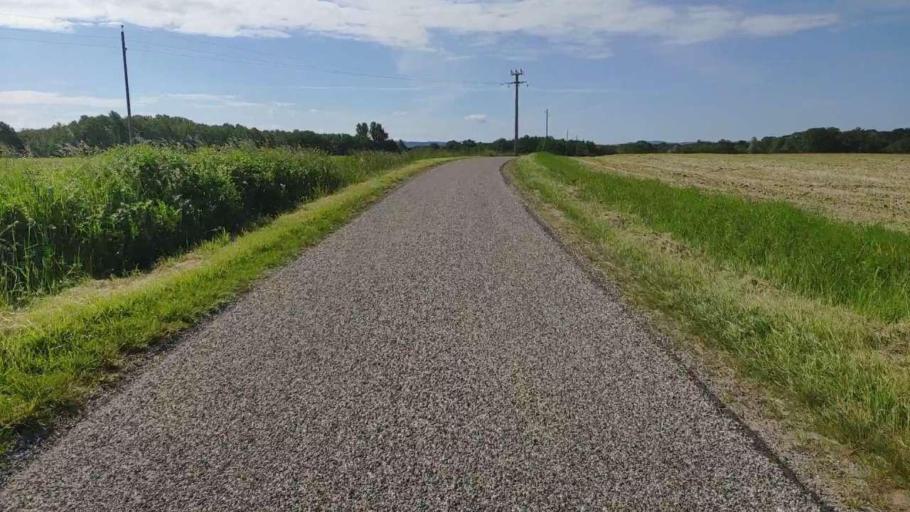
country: FR
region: Franche-Comte
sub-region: Departement du Jura
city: Bletterans
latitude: 46.7055
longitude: 5.4697
